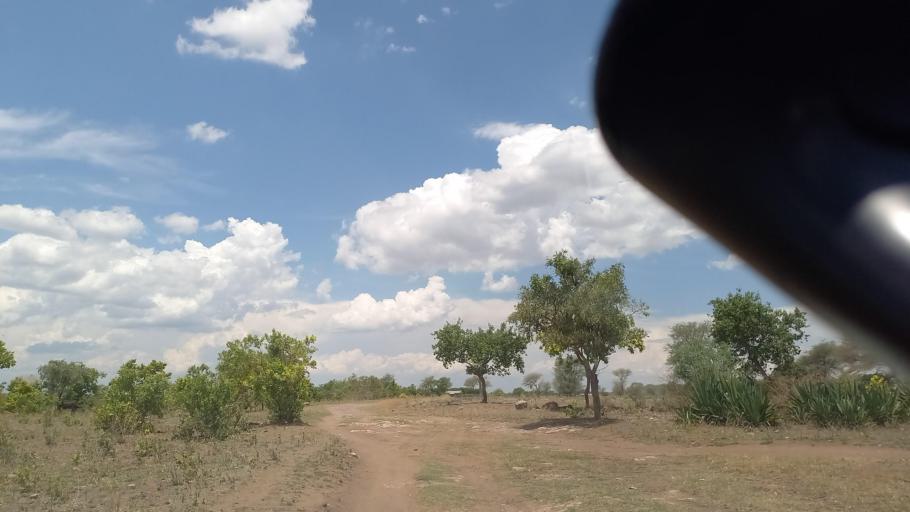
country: ZM
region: Southern
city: Mazabuka
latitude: -16.1100
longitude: 27.8176
